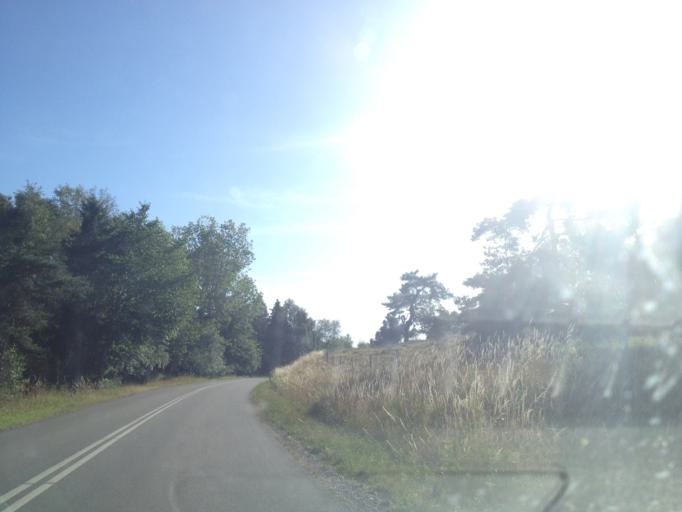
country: DK
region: Capital Region
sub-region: Halsnaes Kommune
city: Frederiksvaerk
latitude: 56.0287
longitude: 12.1002
